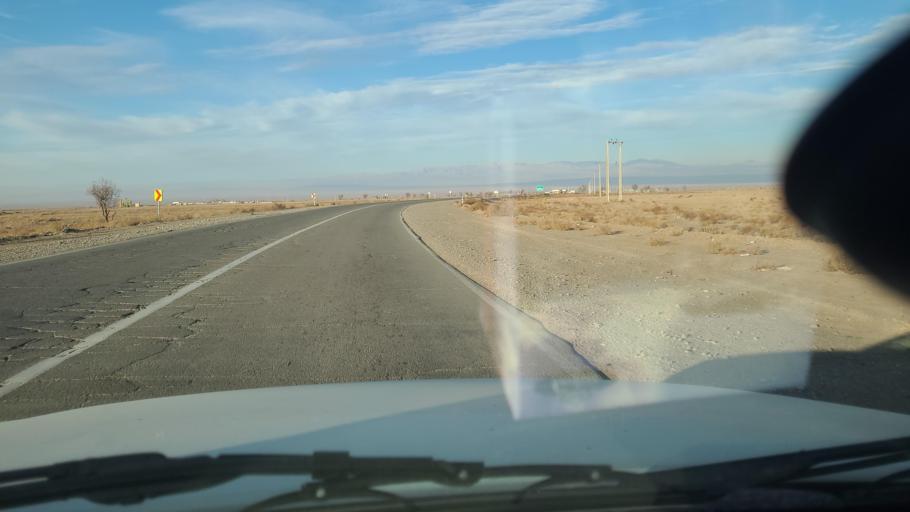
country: IR
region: Razavi Khorasan
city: Neqab
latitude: 36.4989
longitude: 57.5310
